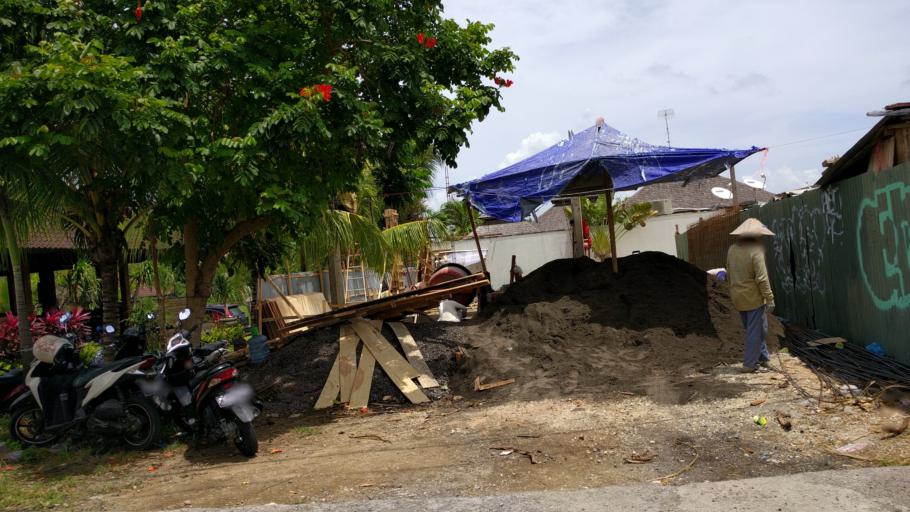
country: ID
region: Bali
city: Banjar Gunungpande
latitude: -8.6681
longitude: 115.1471
